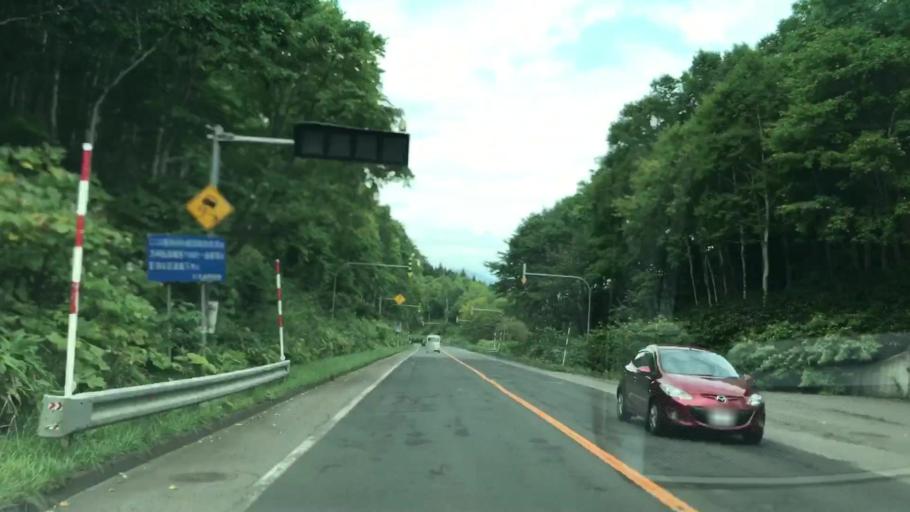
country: JP
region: Hokkaido
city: Niseko Town
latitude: 42.9250
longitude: 140.7177
